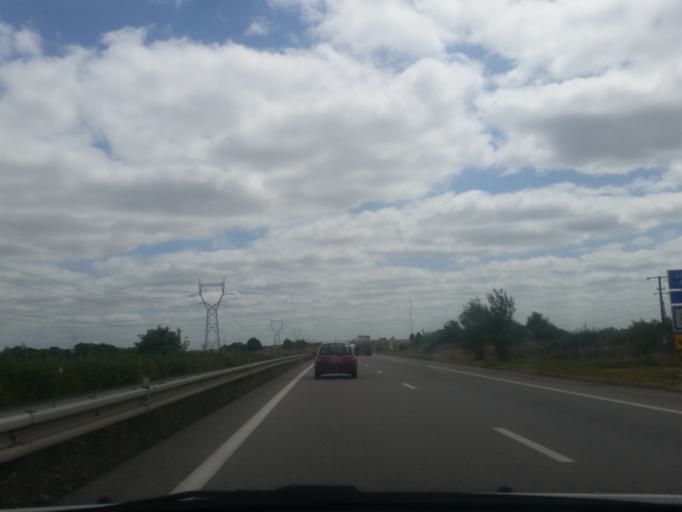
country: FR
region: Pays de la Loire
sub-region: Departement de la Loire-Atlantique
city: Varades
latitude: 47.4217
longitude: -1.0355
